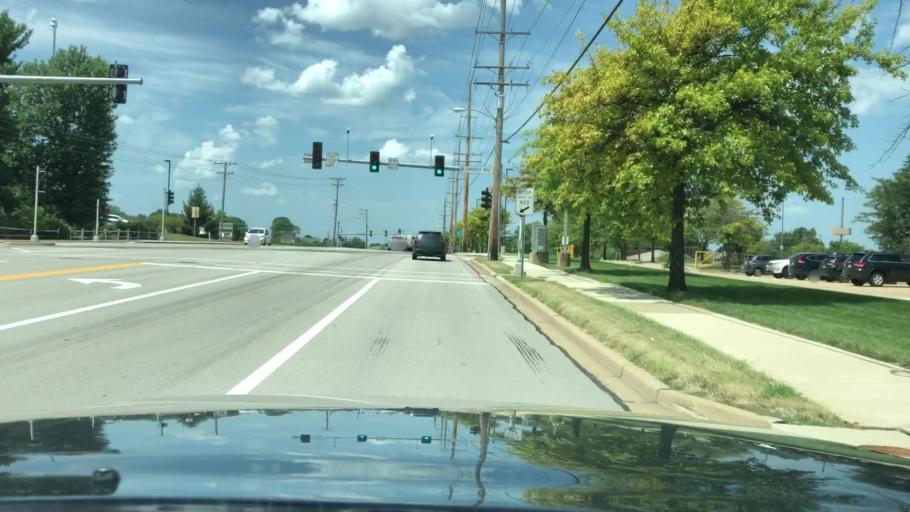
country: US
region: Missouri
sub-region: Saint Charles County
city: O'Fallon
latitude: 38.7878
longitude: -90.6694
